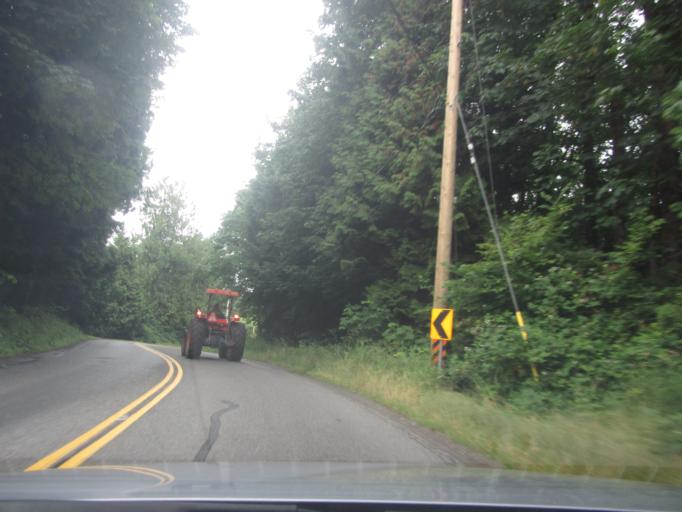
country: CA
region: British Columbia
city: Aldergrove
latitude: 49.1040
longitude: -122.3694
